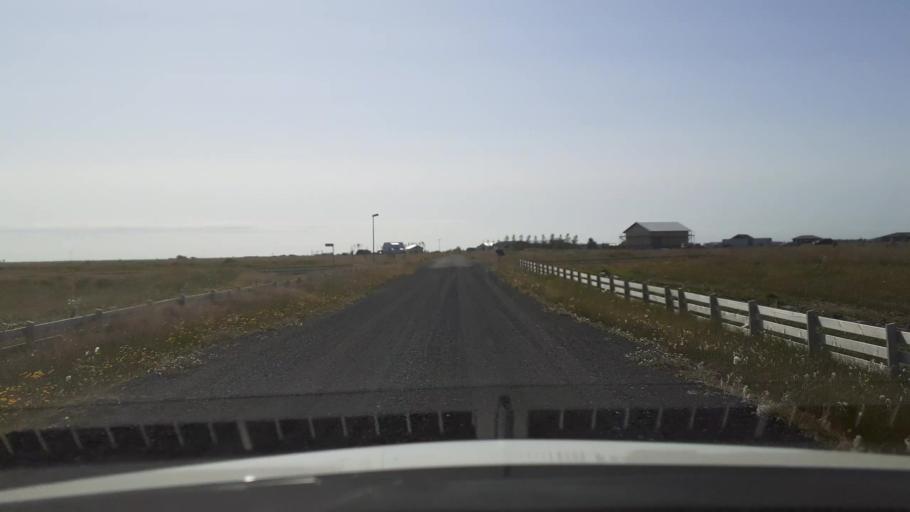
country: IS
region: South
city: Selfoss
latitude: 63.8991
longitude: -21.0811
